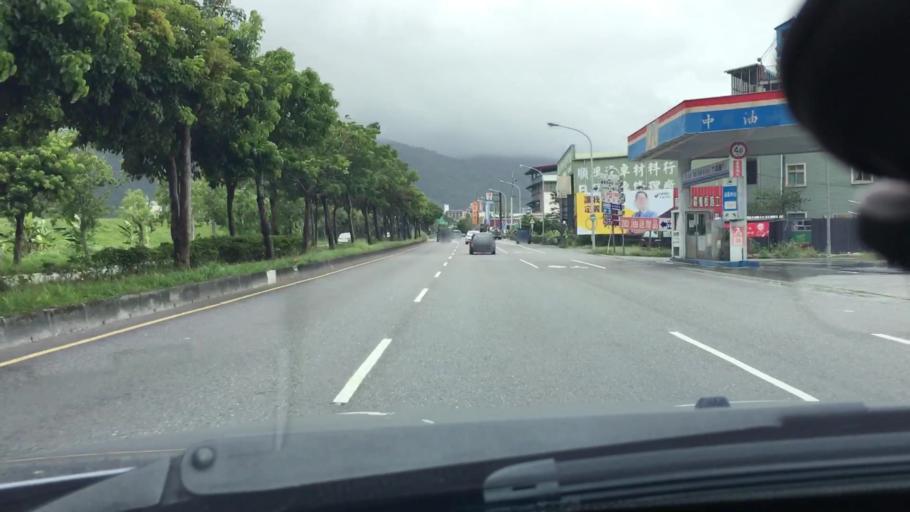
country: TW
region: Taiwan
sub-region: Yilan
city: Yilan
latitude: 24.8112
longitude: 121.7673
